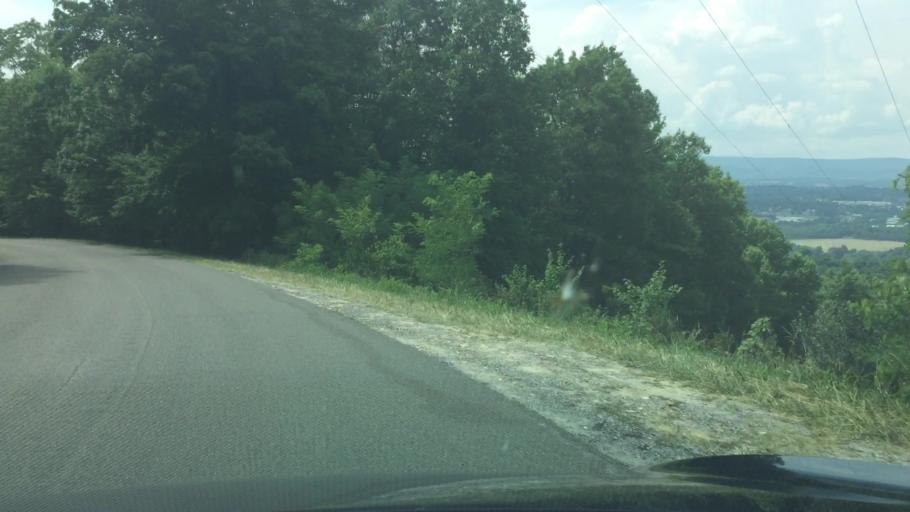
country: US
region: Virginia
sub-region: Wythe County
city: Wytheville
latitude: 36.9247
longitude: -81.0491
